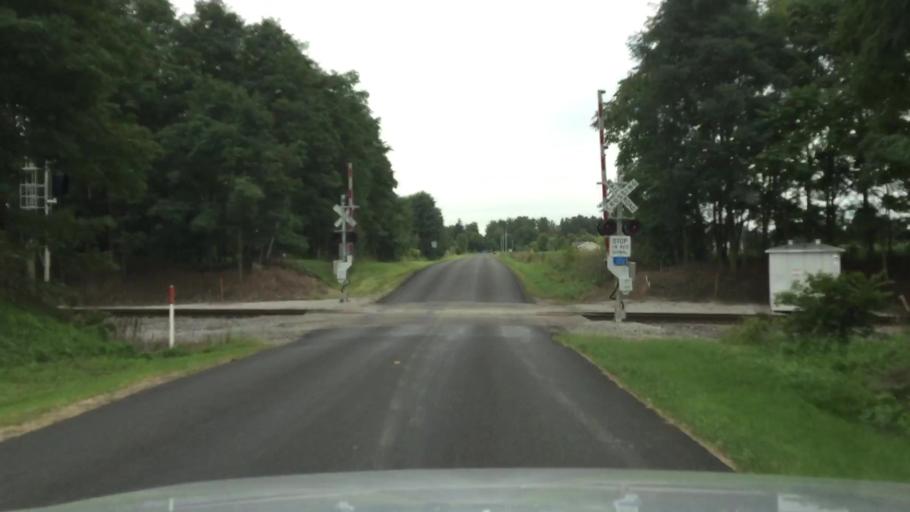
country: US
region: Michigan
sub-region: Shiawassee County
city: Durand
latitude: 42.8776
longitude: -84.0622
